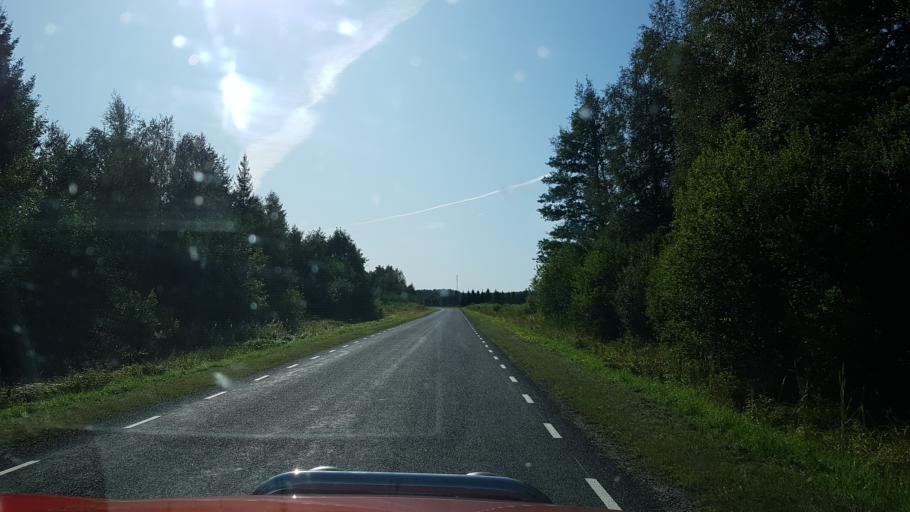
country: LV
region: Salacgrivas
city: Ainazi
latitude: 58.0788
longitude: 24.5330
